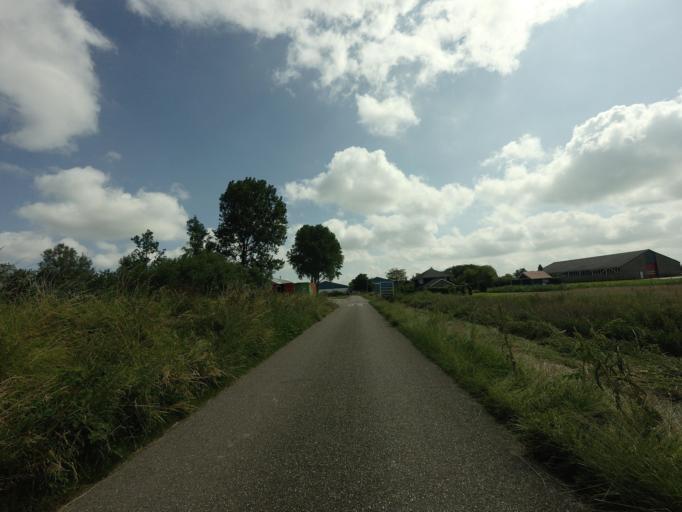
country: NL
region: North Holland
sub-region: Gemeente Schagen
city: Schagen
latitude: 52.8571
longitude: 4.8369
